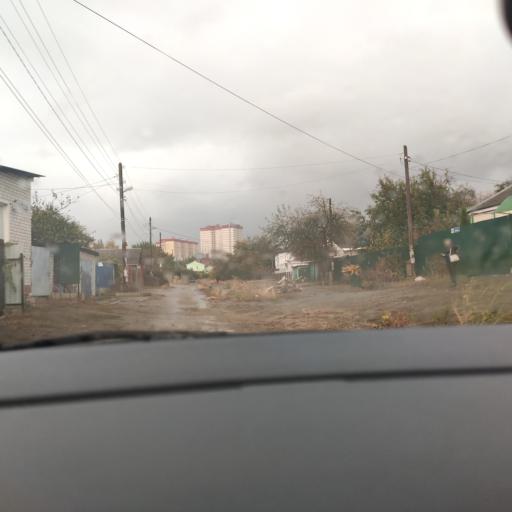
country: RU
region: Voronezj
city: Voronezh
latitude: 51.6717
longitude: 39.1437
